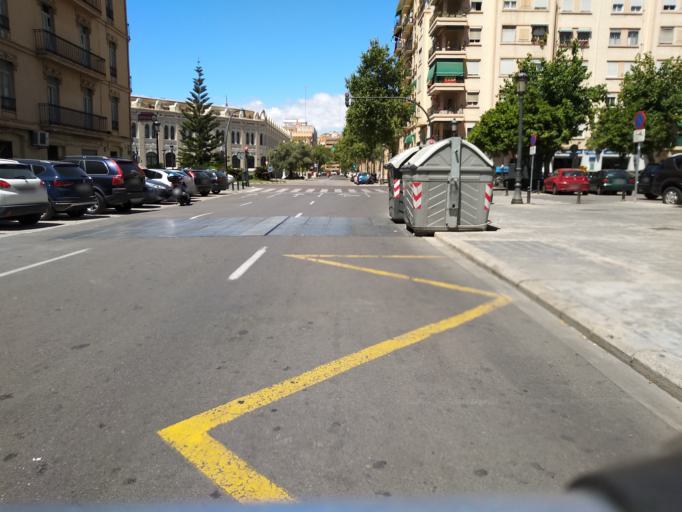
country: ES
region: Valencia
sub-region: Provincia de Valencia
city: Valencia
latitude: 39.4730
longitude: -0.3595
